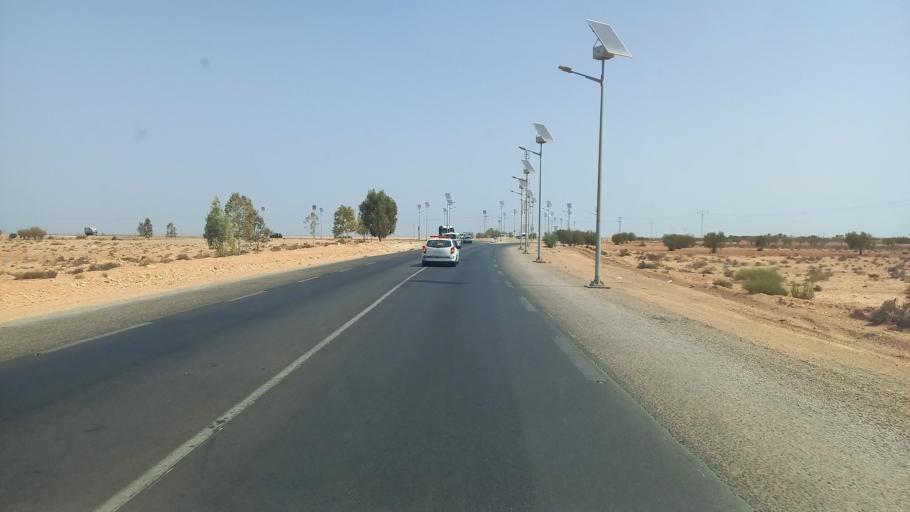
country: TN
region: Madanin
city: Medenine
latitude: 33.3840
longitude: 10.7010
